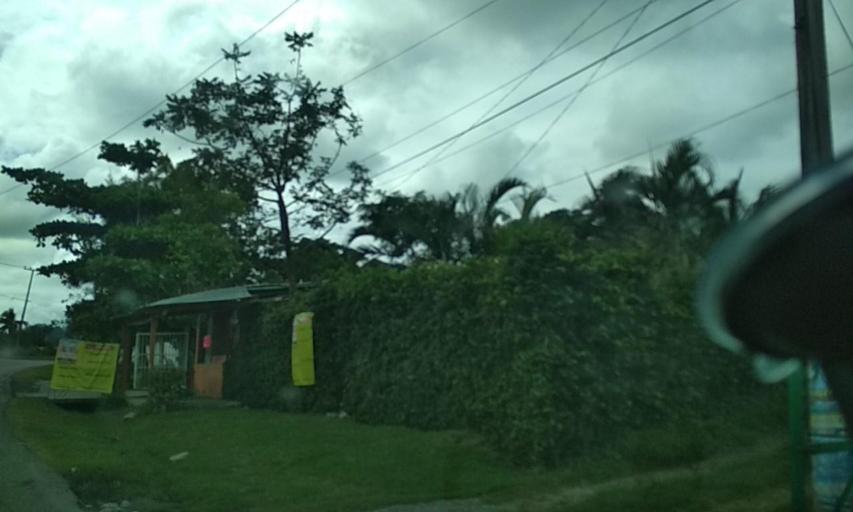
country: MX
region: Veracruz
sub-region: Papantla
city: Residencial Tajin
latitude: 20.6361
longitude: -97.3701
